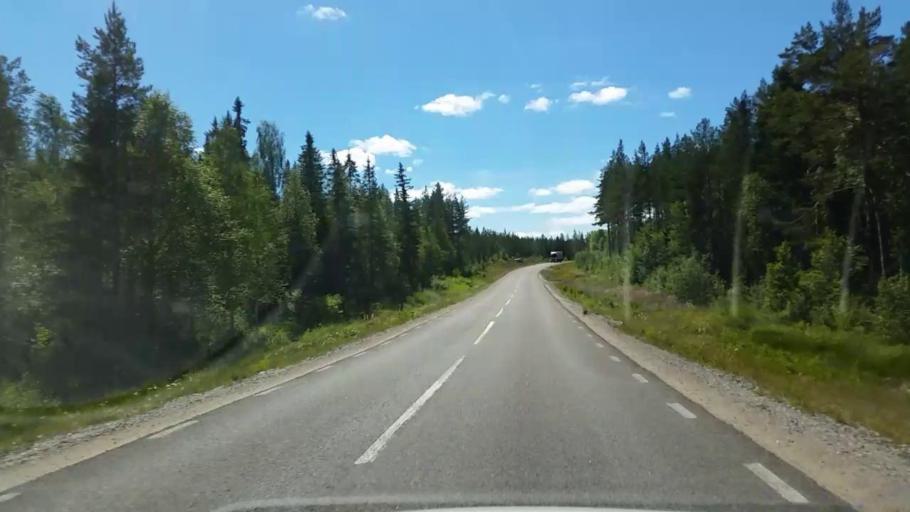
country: SE
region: Gaevleborg
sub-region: Ljusdals Kommun
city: Farila
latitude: 61.6304
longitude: 15.5761
